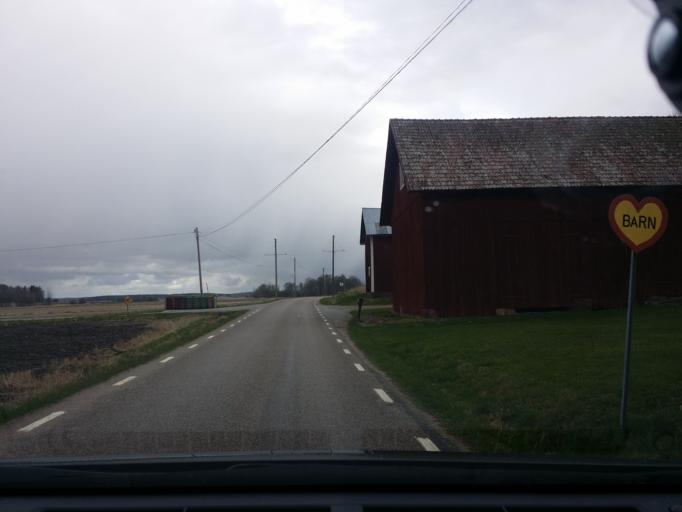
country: SE
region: Uppsala
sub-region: Enkopings Kommun
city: Enkoping
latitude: 59.6705
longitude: 17.0254
